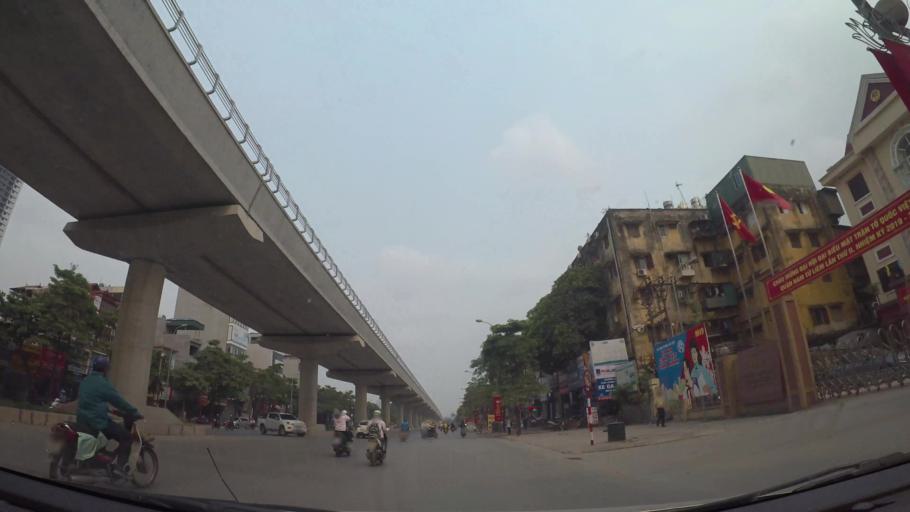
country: VN
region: Ha Noi
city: Cau Dien
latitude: 21.0401
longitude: 105.7654
